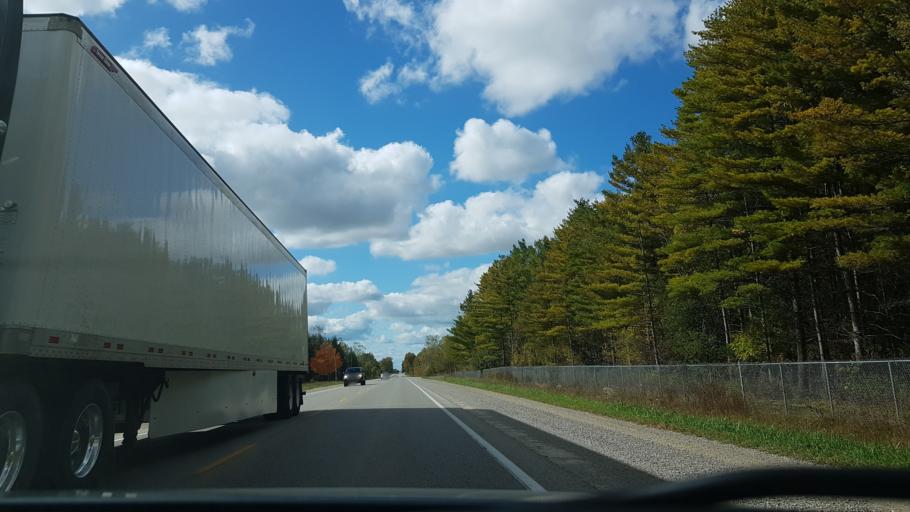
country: CA
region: Ontario
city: South Huron
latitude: 43.3567
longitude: -81.5316
